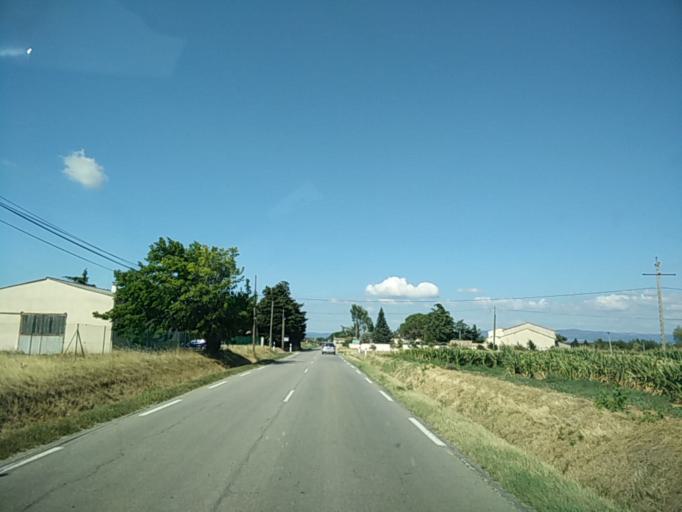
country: FR
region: Rhone-Alpes
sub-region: Departement de la Drome
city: La Begude-de-Mazenc
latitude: 44.5531
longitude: 4.8864
